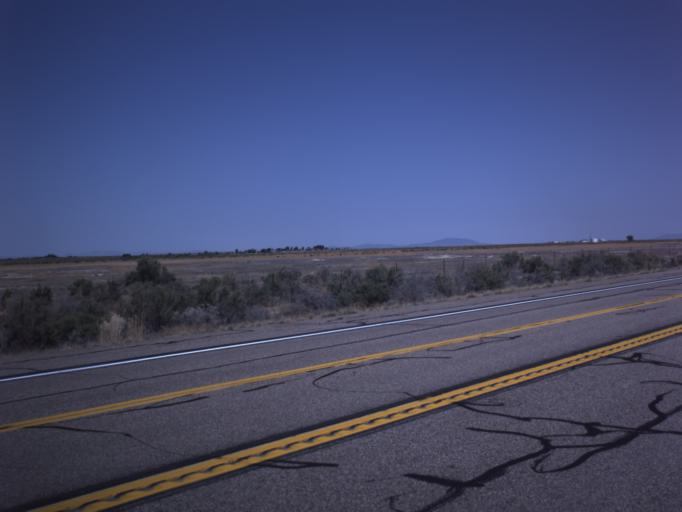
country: US
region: Utah
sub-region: Millard County
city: Delta
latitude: 39.3563
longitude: -112.4965
